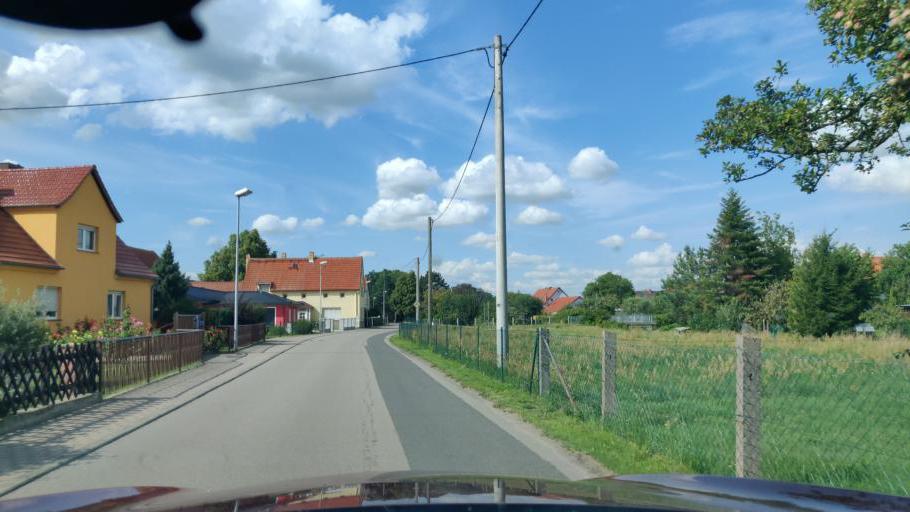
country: DE
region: Saxony
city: Schildau
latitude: 51.4943
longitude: 12.8994
